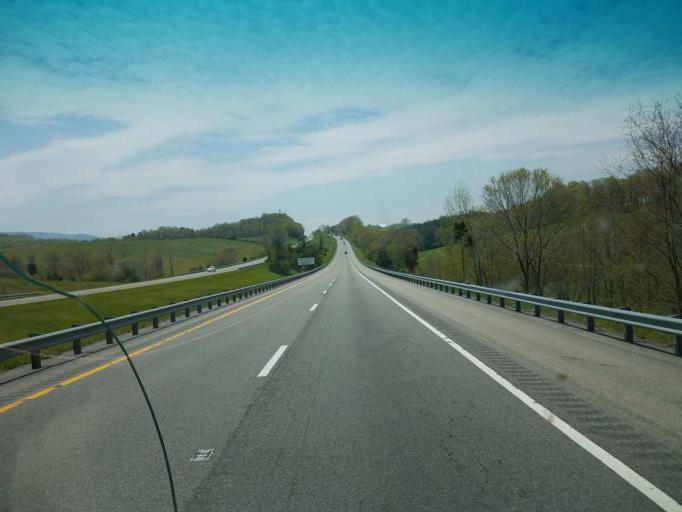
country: US
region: Virginia
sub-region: Wythe County
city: Rural Retreat
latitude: 36.9108
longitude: -81.2945
